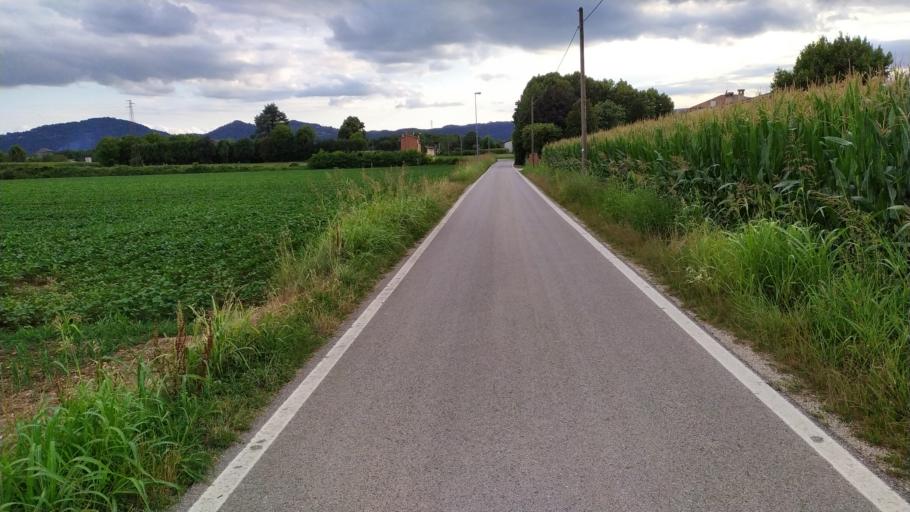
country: IT
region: Veneto
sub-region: Provincia di Vicenza
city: Villaverla
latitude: 45.6511
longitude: 11.4741
